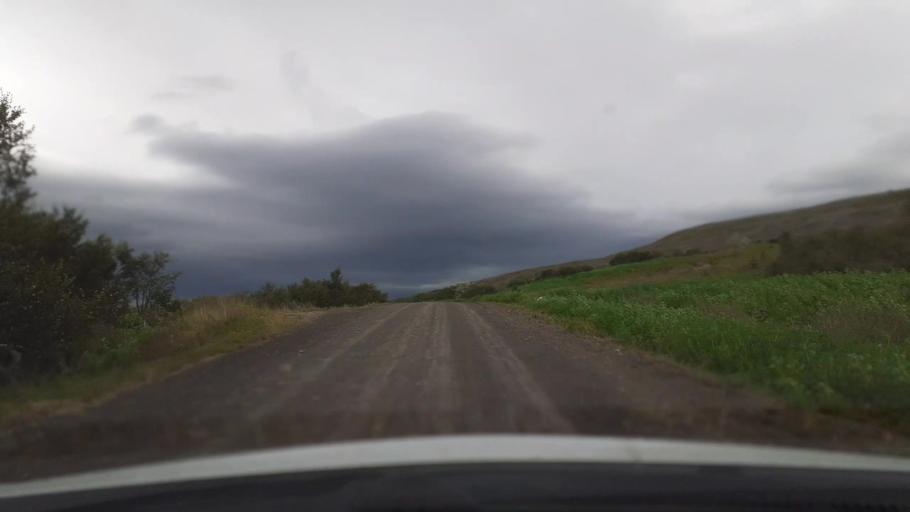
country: IS
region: Capital Region
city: Mosfellsbaer
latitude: 64.5246
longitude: -21.4765
